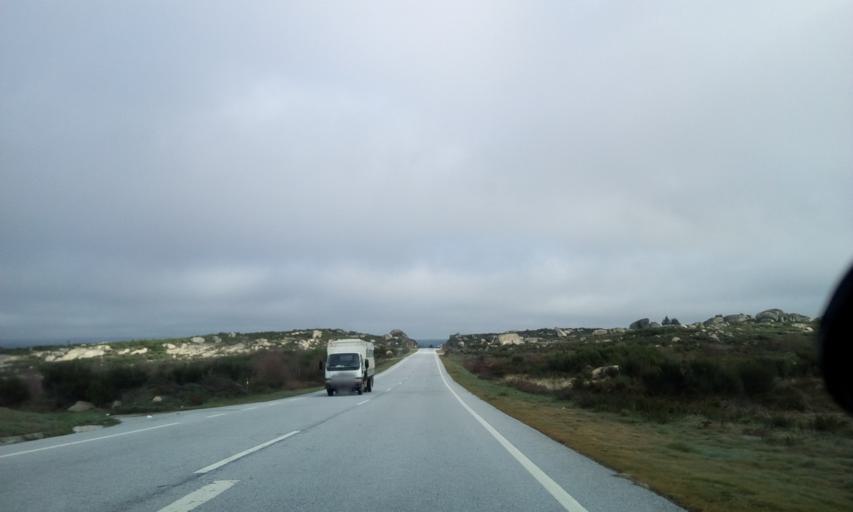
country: PT
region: Guarda
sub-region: Aguiar da Beira
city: Aguiar da Beira
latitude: 40.7636
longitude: -7.5021
